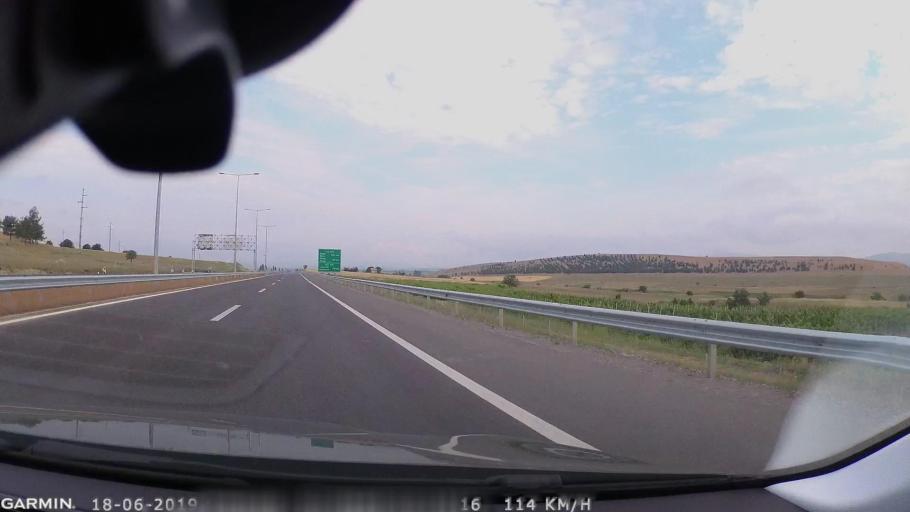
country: MK
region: Stip
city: Shtip
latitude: 41.7842
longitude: 22.1215
